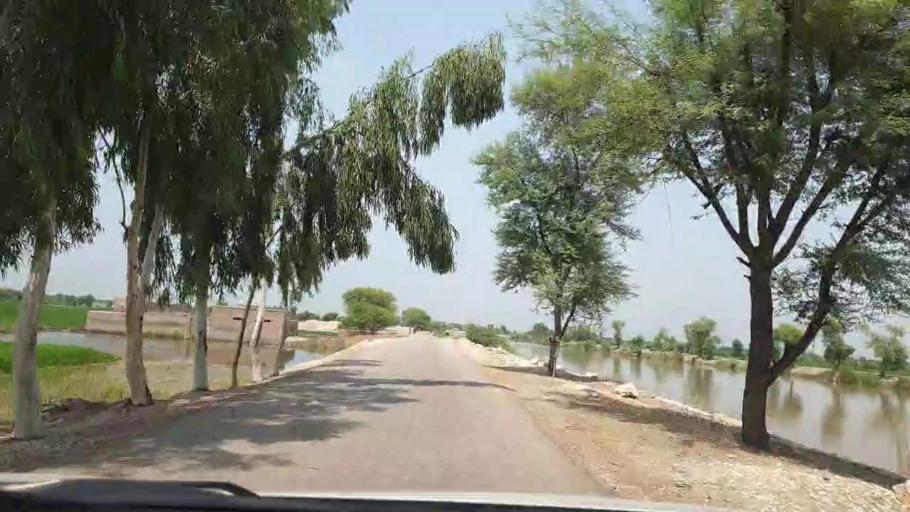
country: PK
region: Sindh
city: Dokri
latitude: 27.3293
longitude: 68.1093
